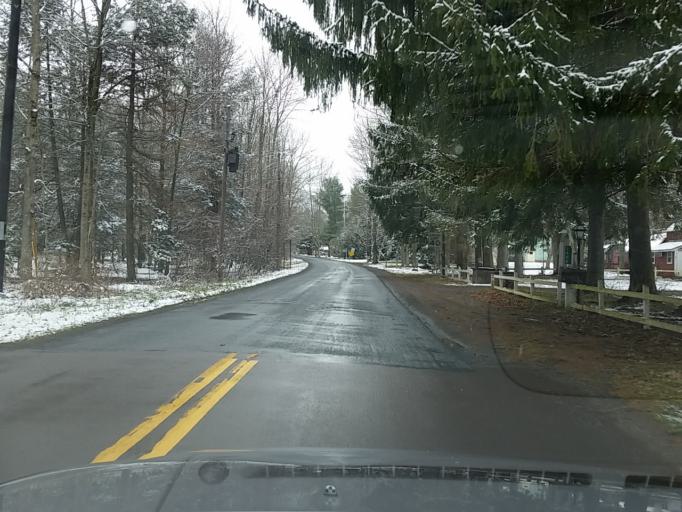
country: US
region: Pennsylvania
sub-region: Sullivan County
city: Laporte
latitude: 41.3056
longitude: -76.4090
